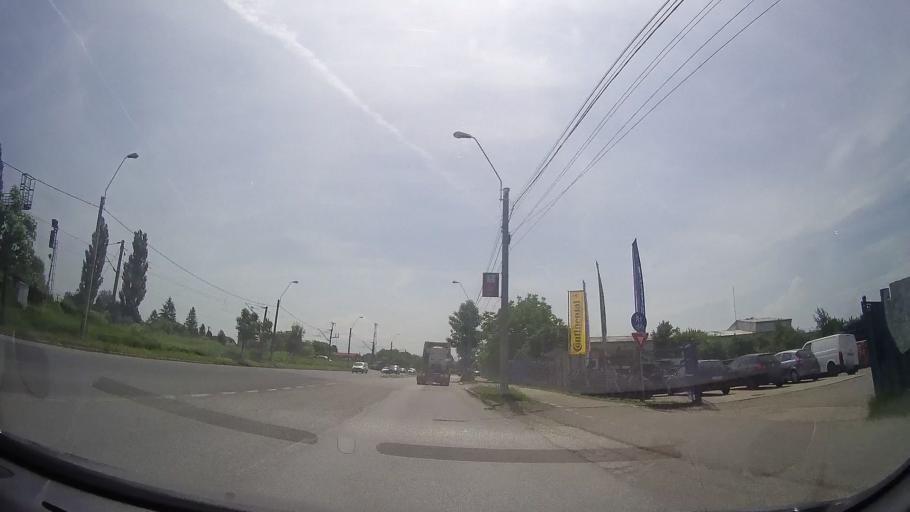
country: RO
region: Hunedoara
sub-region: Municipiul Deva
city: Deva
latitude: 45.8927
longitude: 22.9034
